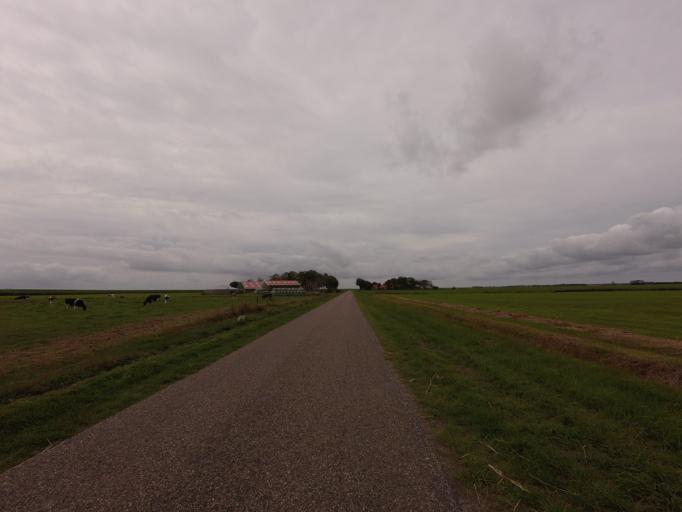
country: NL
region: Friesland
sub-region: Gemeente Ameland
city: Hollum
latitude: 53.4348
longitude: 5.7052
